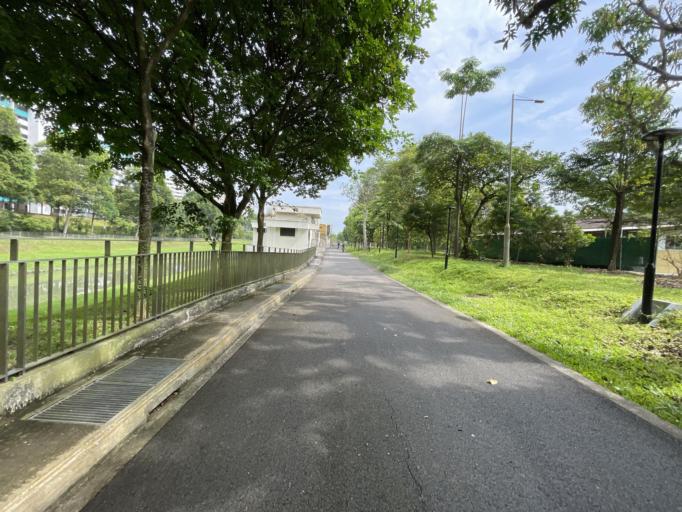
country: SG
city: Singapore
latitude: 1.3197
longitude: 103.7704
